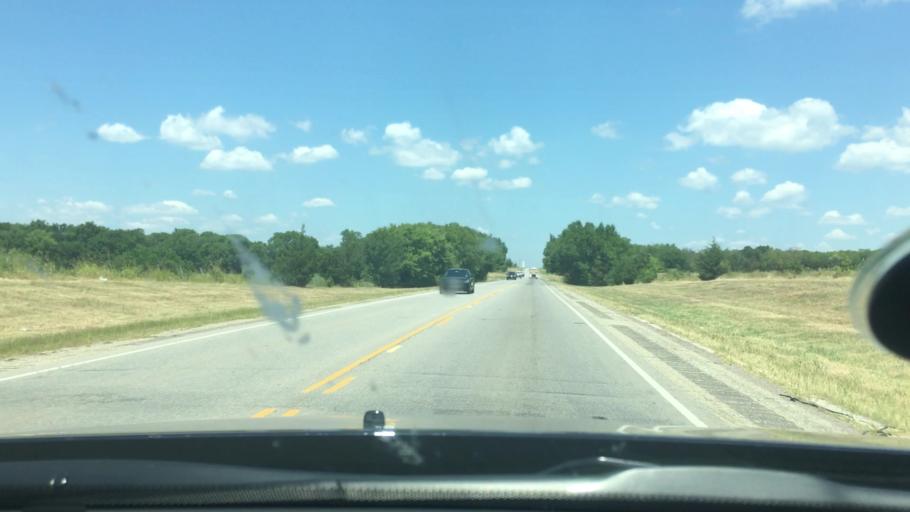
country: US
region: Oklahoma
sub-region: Marshall County
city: Oakland
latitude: 34.1221
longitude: -96.7821
